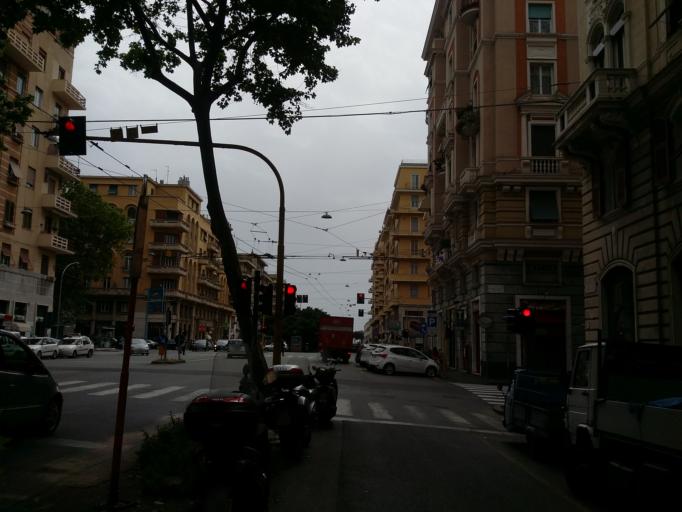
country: IT
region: Liguria
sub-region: Provincia di Genova
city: San Teodoro
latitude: 44.3985
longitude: 8.9489
